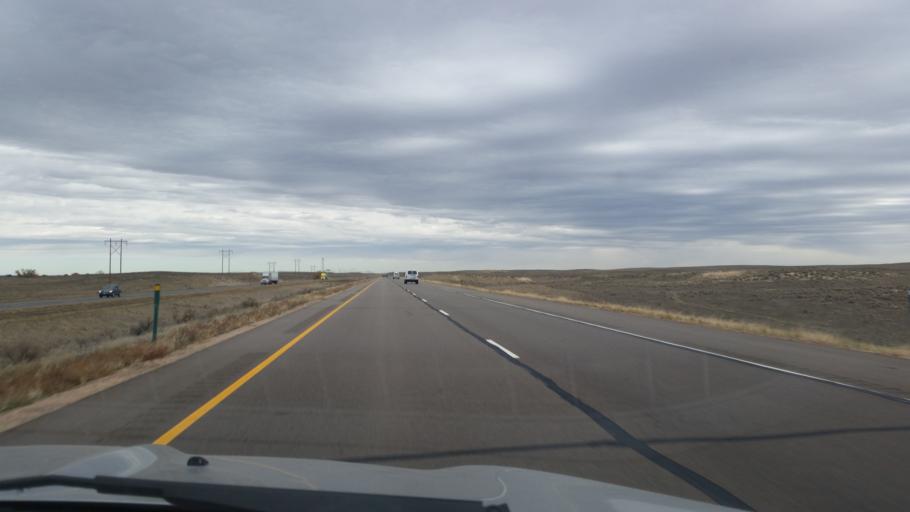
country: US
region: Colorado
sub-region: Morgan County
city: Brush
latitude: 40.3199
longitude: -103.4953
